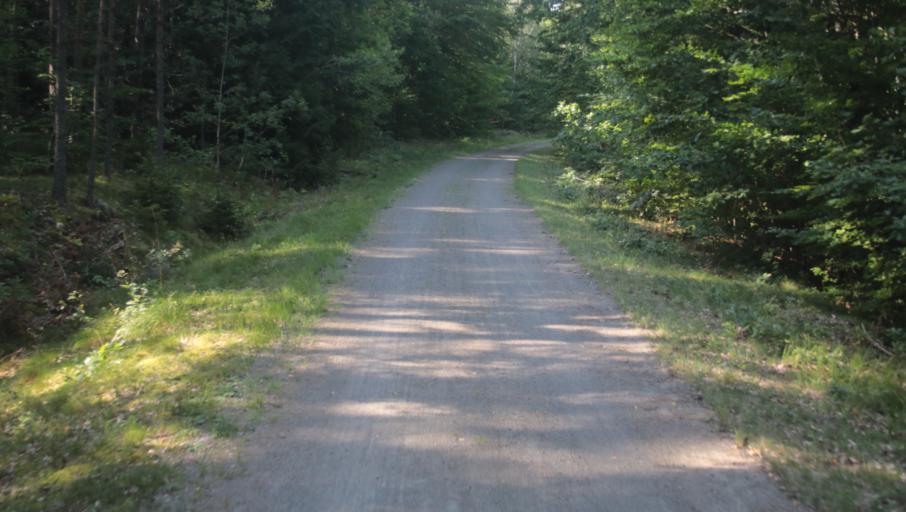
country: SE
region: Blekinge
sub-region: Karlshamns Kommun
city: Svangsta
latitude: 56.2824
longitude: 14.7538
